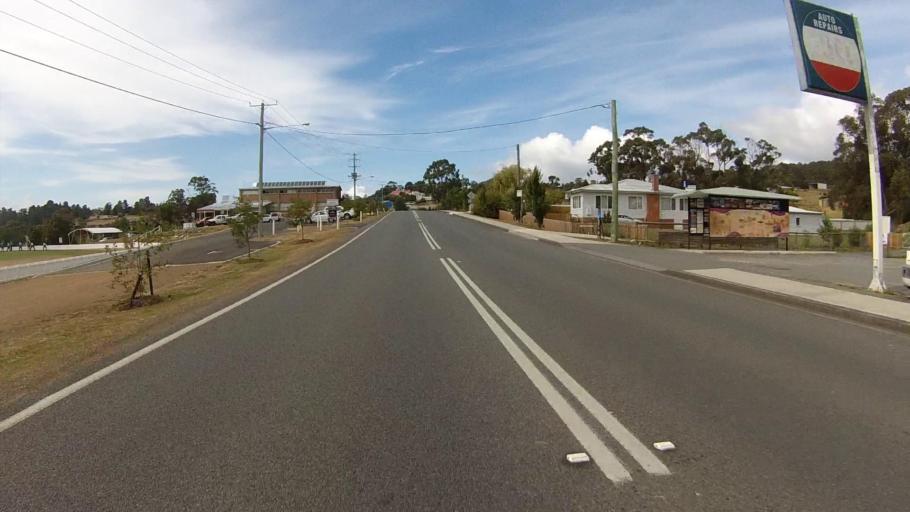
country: AU
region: Tasmania
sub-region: Kingborough
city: Kettering
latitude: -43.1242
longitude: 147.2453
